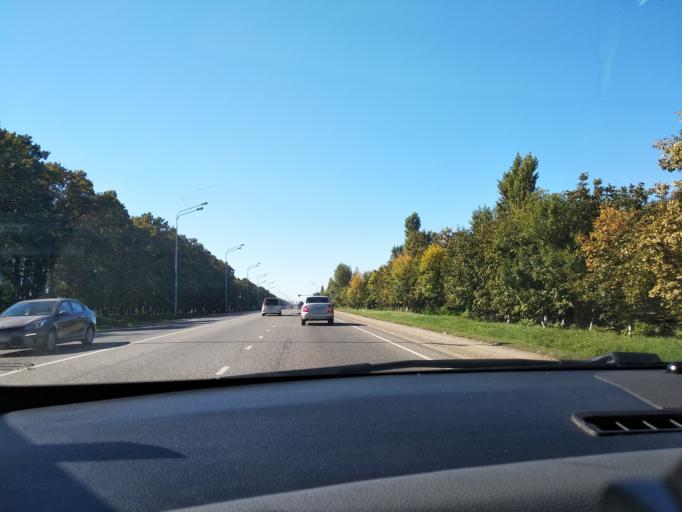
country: RU
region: Krasnodarskiy
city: Novotitarovskaya
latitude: 45.1449
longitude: 39.0475
